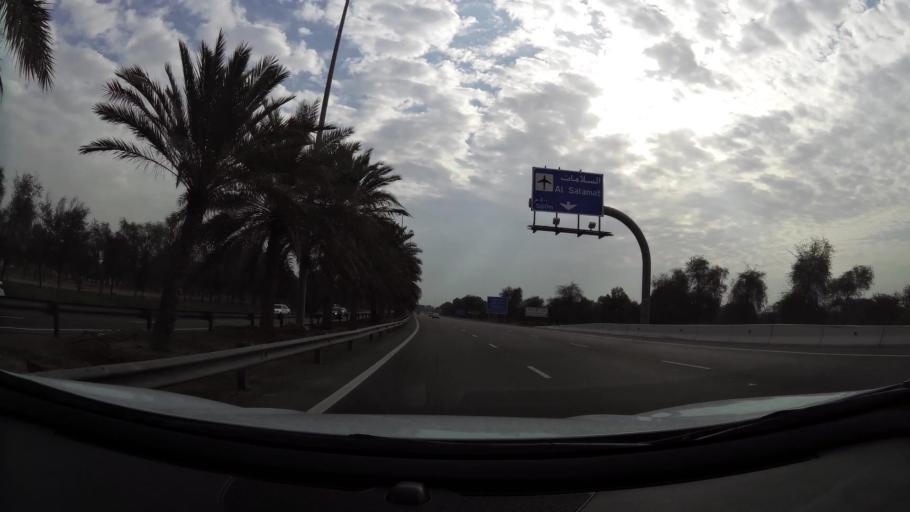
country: AE
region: Abu Dhabi
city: Al Ain
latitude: 24.2019
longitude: 55.5713
